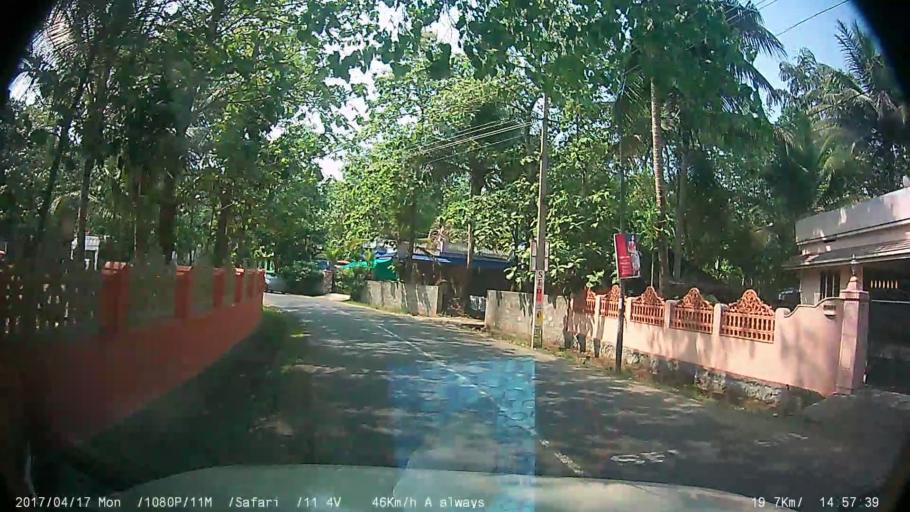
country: IN
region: Kerala
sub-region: Ernakulam
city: Piravam
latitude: 9.8320
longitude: 76.5013
